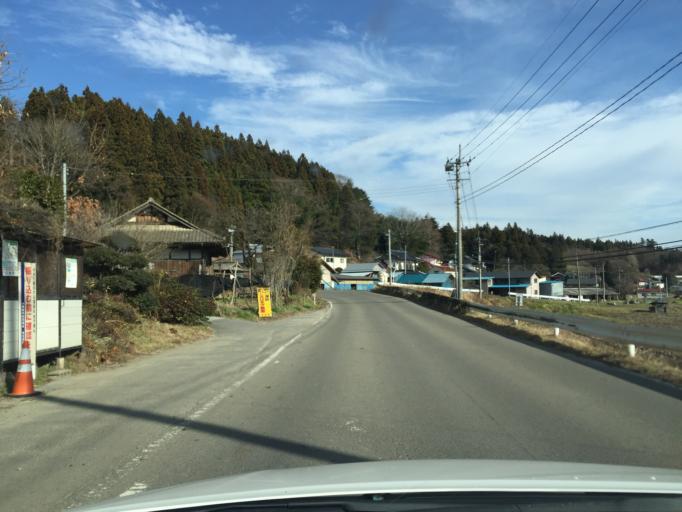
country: JP
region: Fukushima
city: Funehikimachi-funehiki
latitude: 37.2791
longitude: 140.6134
